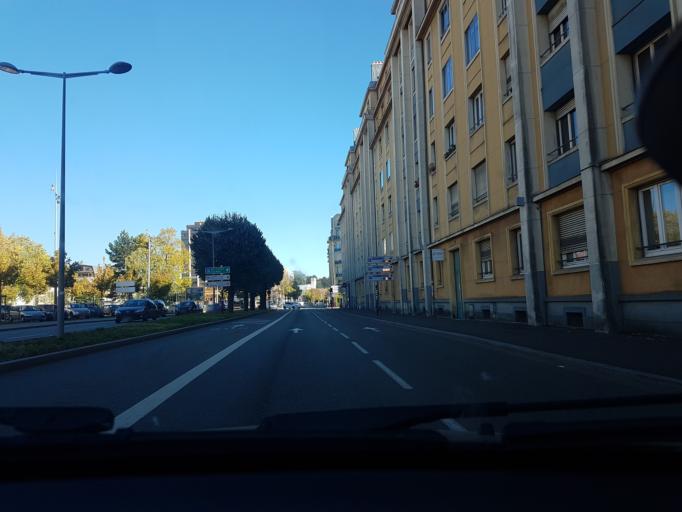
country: FR
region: Franche-Comte
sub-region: Territoire de Belfort
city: Belfort
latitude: 47.6413
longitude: 6.8543
